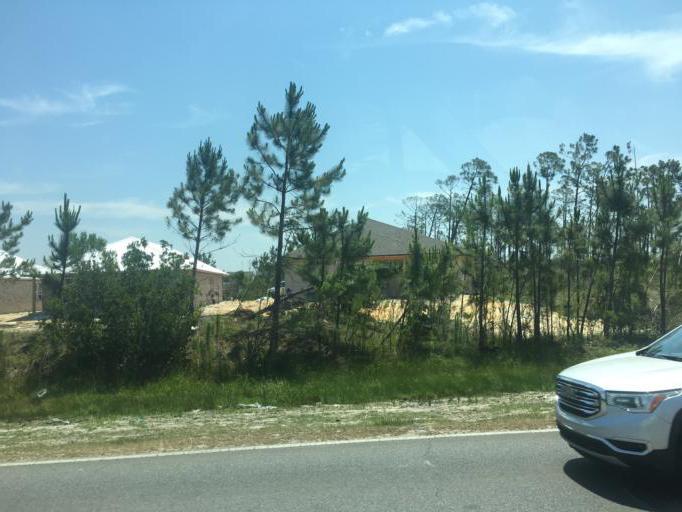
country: US
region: Florida
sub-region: Bay County
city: Lynn Haven
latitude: 30.2172
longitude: -85.6622
